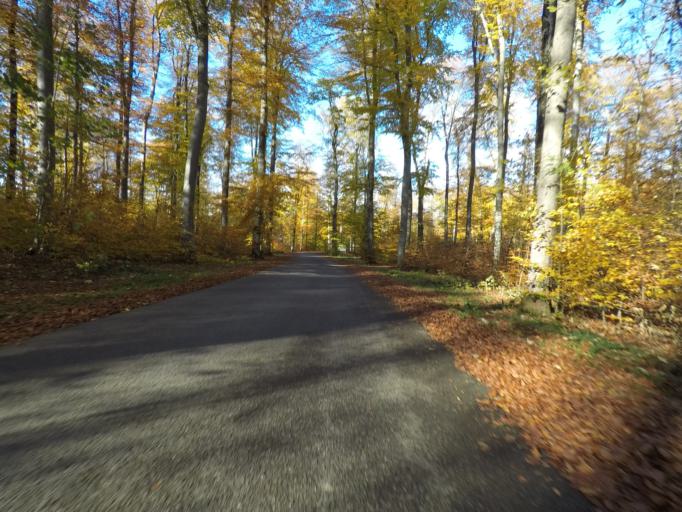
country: DE
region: Baden-Wuerttemberg
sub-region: Tuebingen Region
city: Pfullingen
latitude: 48.4155
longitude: 9.2216
